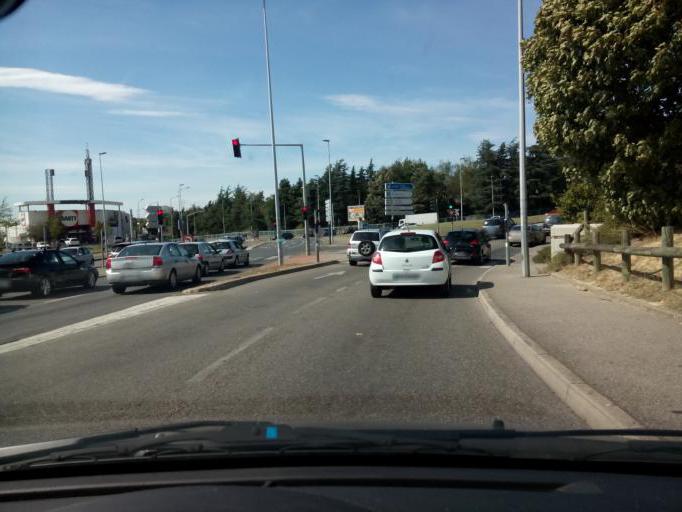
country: FR
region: Rhone-Alpes
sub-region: Departement du Rhone
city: Bron
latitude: 45.7223
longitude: 4.9210
